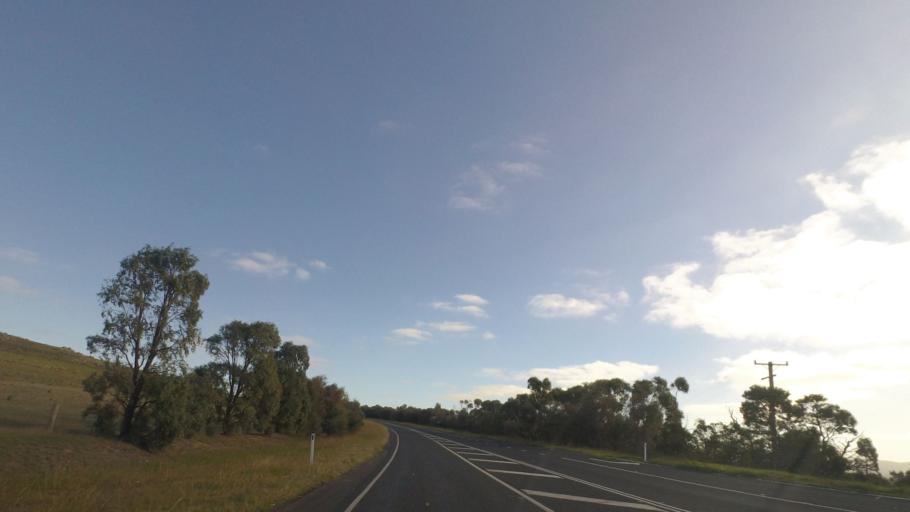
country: AU
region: Victoria
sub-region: Hume
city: Sunbury
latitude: -37.5334
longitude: 144.6701
